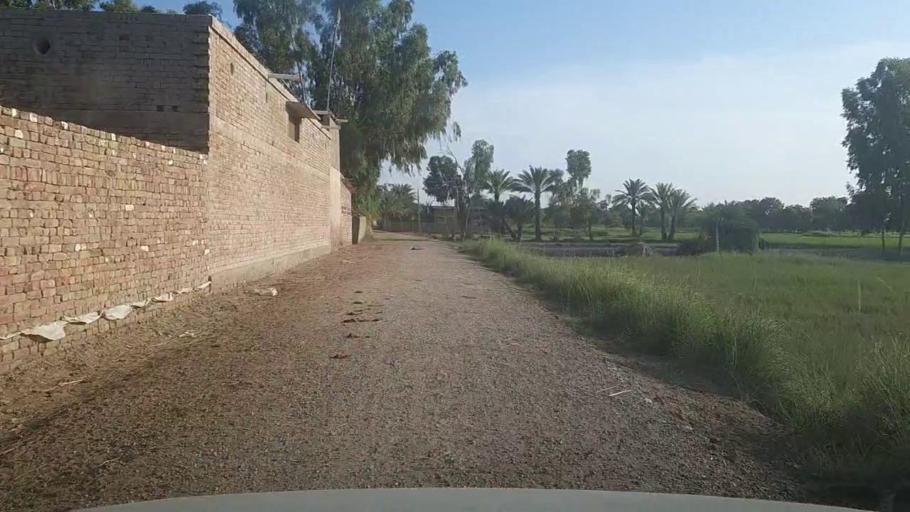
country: PK
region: Sindh
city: Khairpur
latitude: 28.0894
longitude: 69.6394
